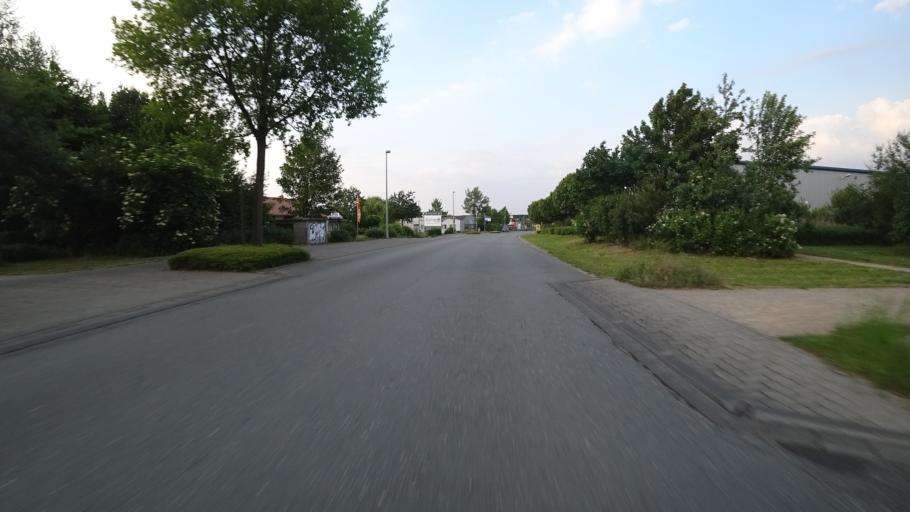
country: DE
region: North Rhine-Westphalia
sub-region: Regierungsbezirk Arnsberg
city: Lippstadt
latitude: 51.6518
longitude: 8.3526
